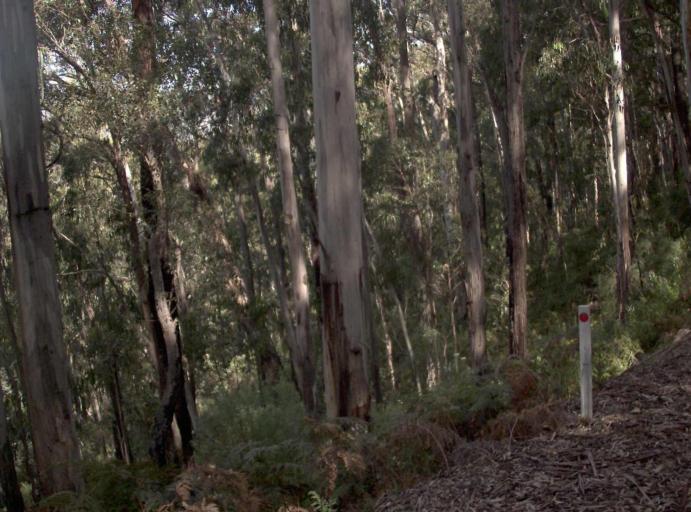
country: AU
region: Victoria
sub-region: East Gippsland
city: Lakes Entrance
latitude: -37.3998
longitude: 148.1250
